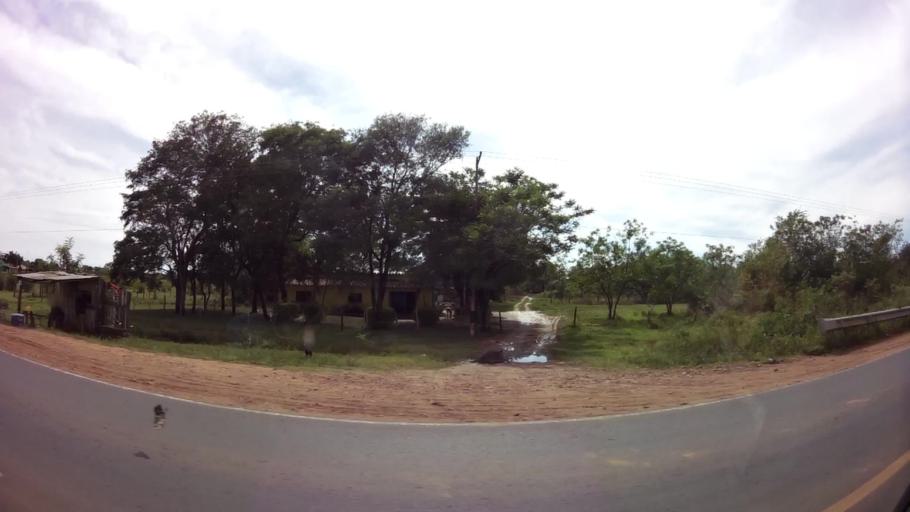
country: PY
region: Central
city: Limpio
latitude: -25.1365
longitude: -57.4787
